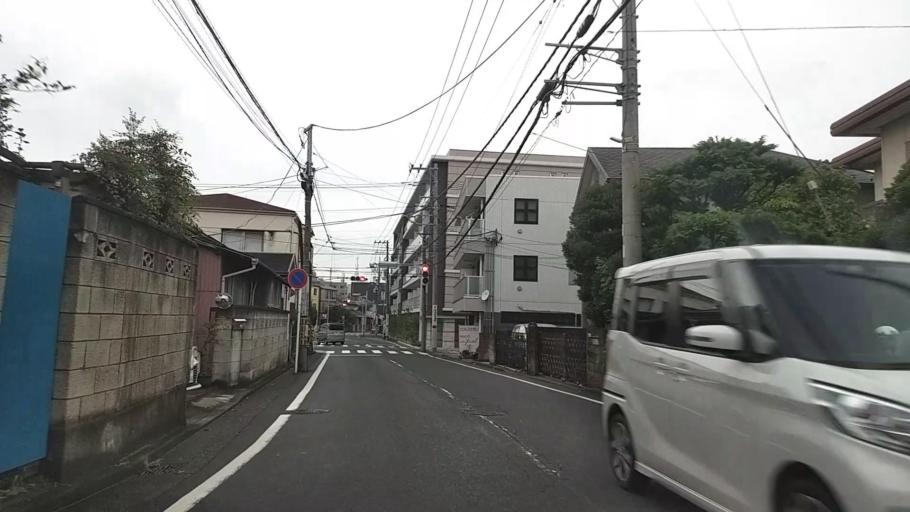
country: JP
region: Kanagawa
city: Yokohama
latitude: 35.4159
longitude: 139.6020
